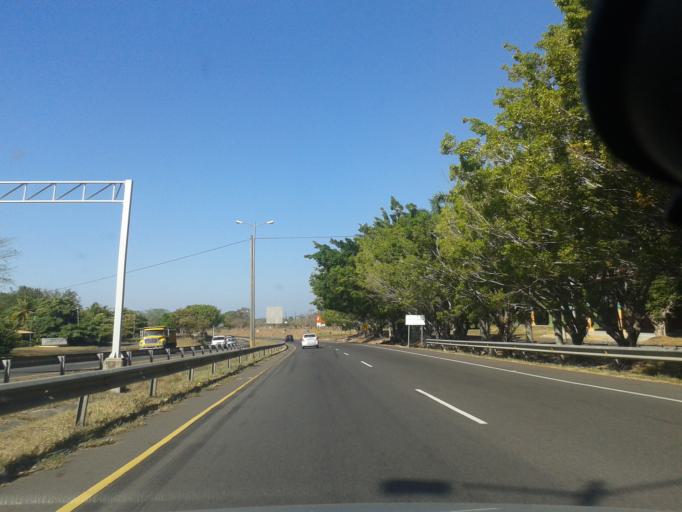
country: CR
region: Alajuela
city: Orotina
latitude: 9.9060
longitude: -84.5237
